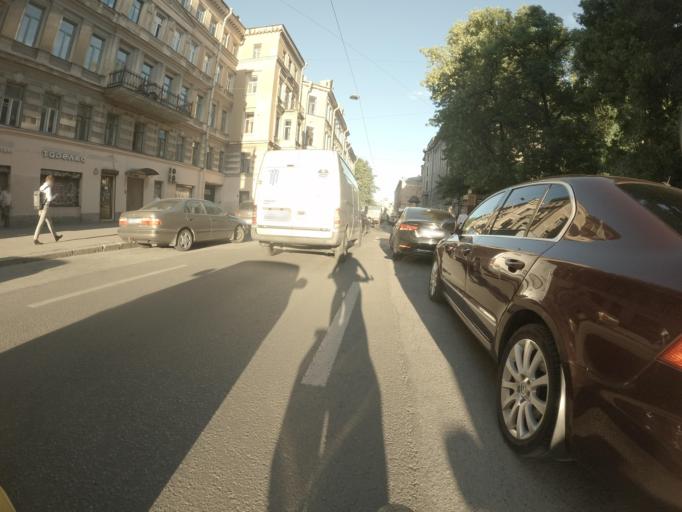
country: RU
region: St.-Petersburg
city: Centralniy
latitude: 59.9272
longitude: 30.3395
